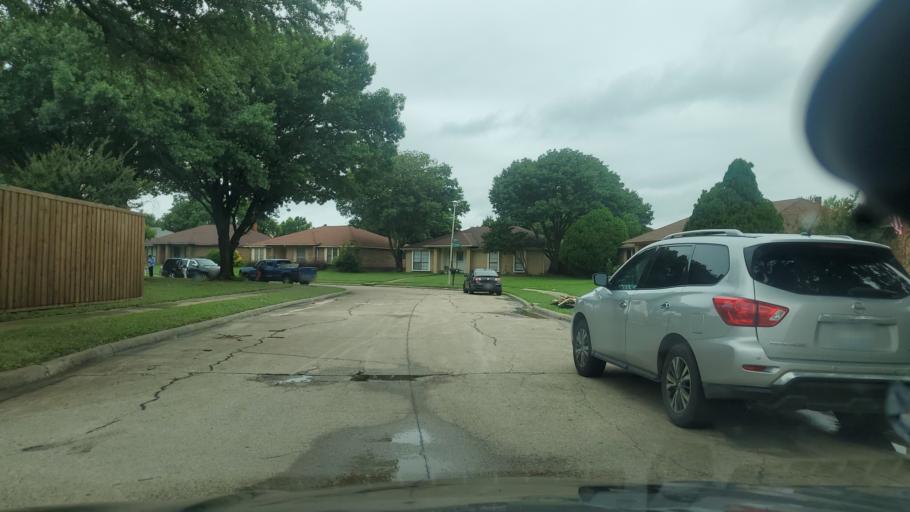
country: US
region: Texas
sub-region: Dallas County
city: Garland
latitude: 32.9403
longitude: -96.6321
